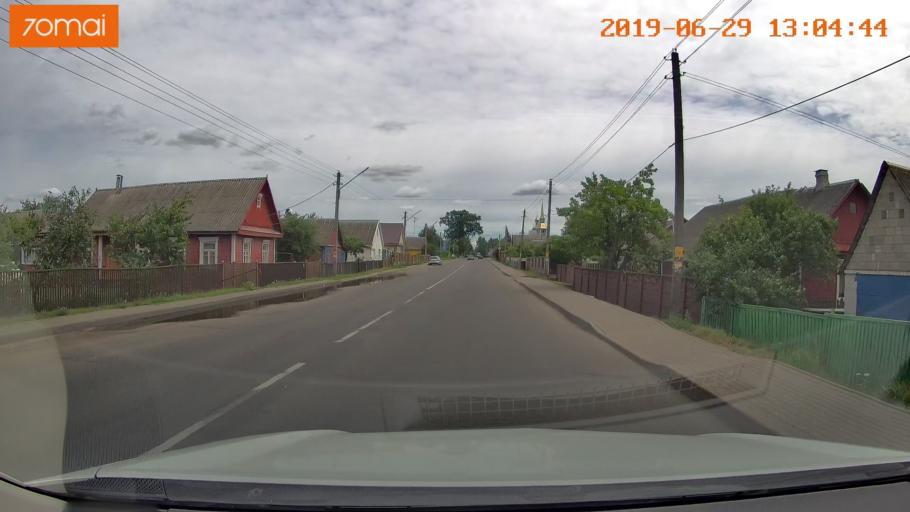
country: BY
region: Minsk
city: Slutsk
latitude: 53.0310
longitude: 27.5749
